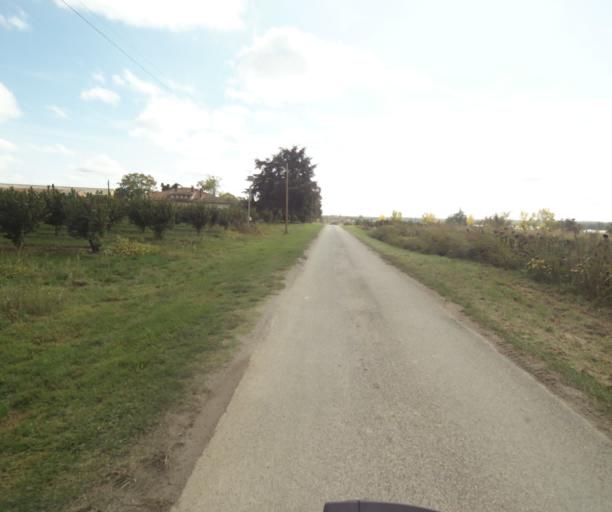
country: FR
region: Midi-Pyrenees
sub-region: Departement du Tarn-et-Garonne
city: Montech
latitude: 43.9504
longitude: 1.2075
